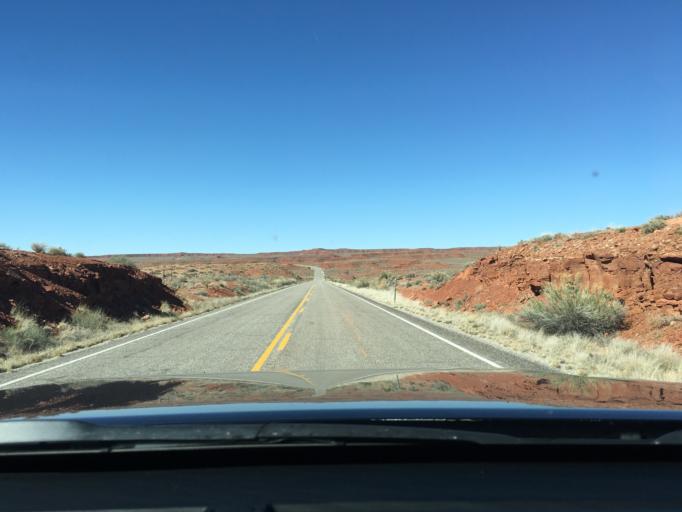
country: US
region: Utah
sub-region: San Juan County
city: Blanding
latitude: 37.2163
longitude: -109.8365
